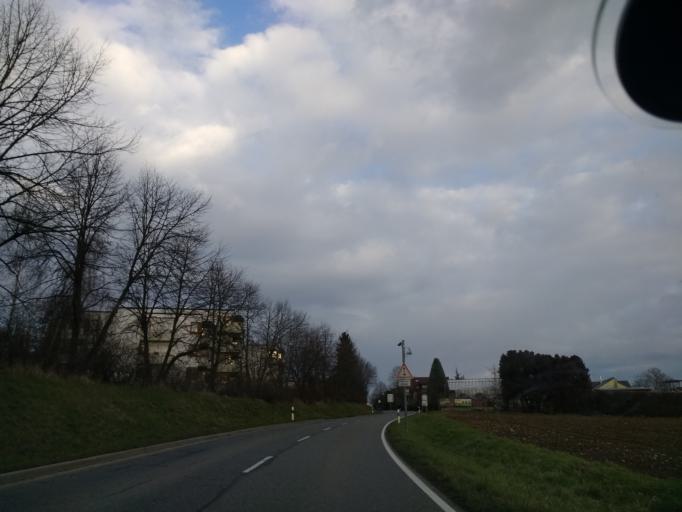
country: DE
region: Baden-Wuerttemberg
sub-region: Freiburg Region
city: Konstanz
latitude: 47.6855
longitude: 9.1978
